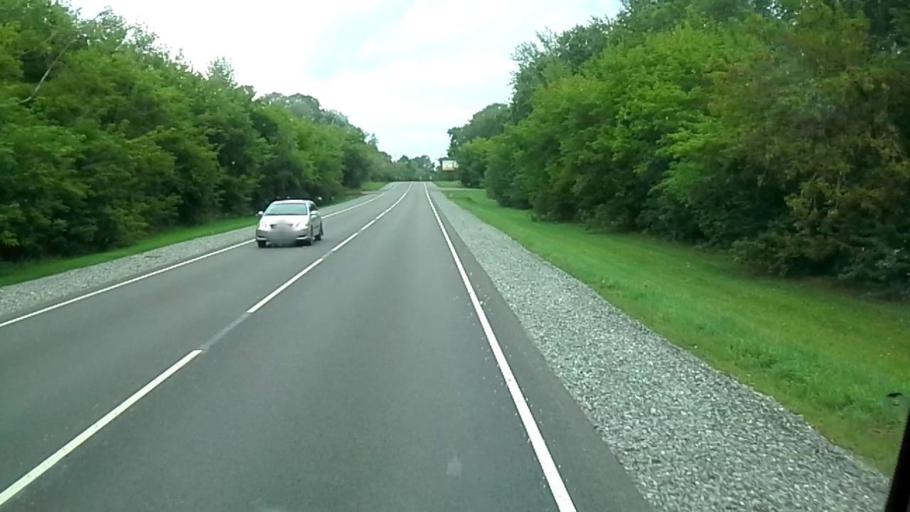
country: RU
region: Altai Krai
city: Srostki
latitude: 52.4289
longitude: 85.6685
